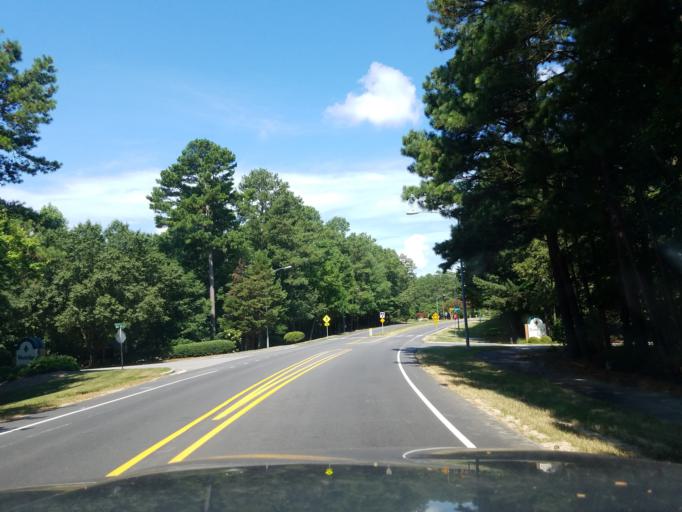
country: US
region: North Carolina
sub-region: Durham County
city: Durham
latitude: 35.9213
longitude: -78.9340
